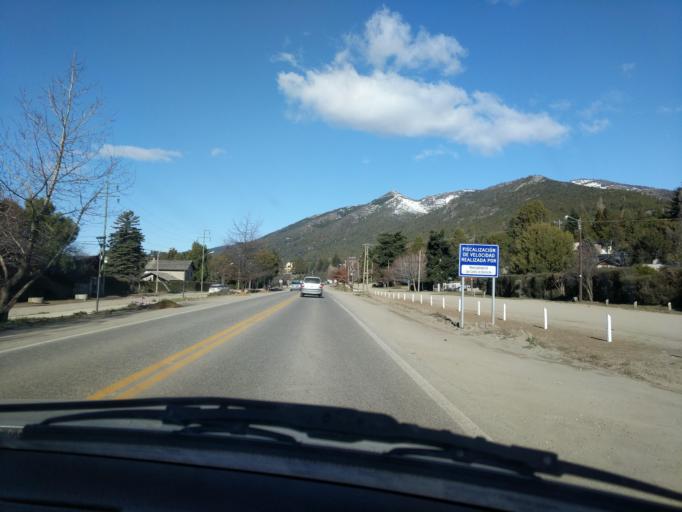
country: AR
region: Rio Negro
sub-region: Departamento de Bariloche
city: San Carlos de Bariloche
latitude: -41.1228
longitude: -71.4033
